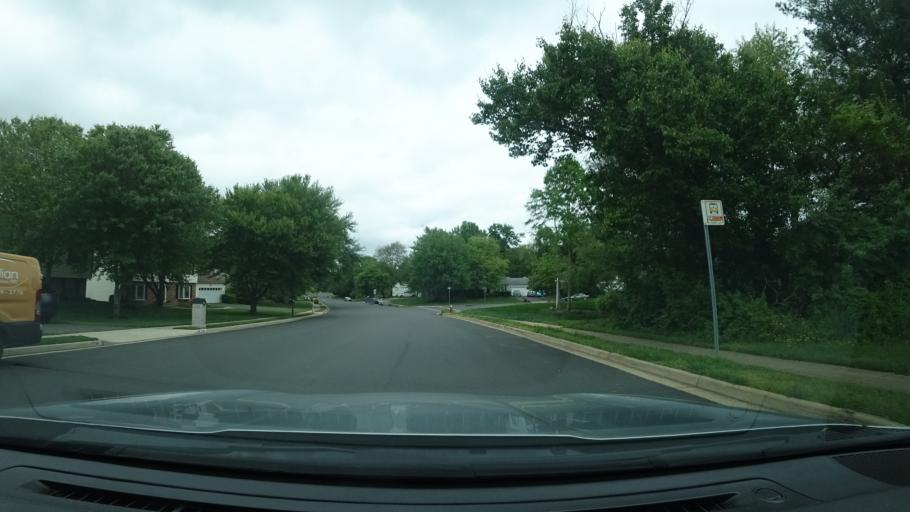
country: US
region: Virginia
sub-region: Fairfax County
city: Oak Hill
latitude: 38.9290
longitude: -77.3830
